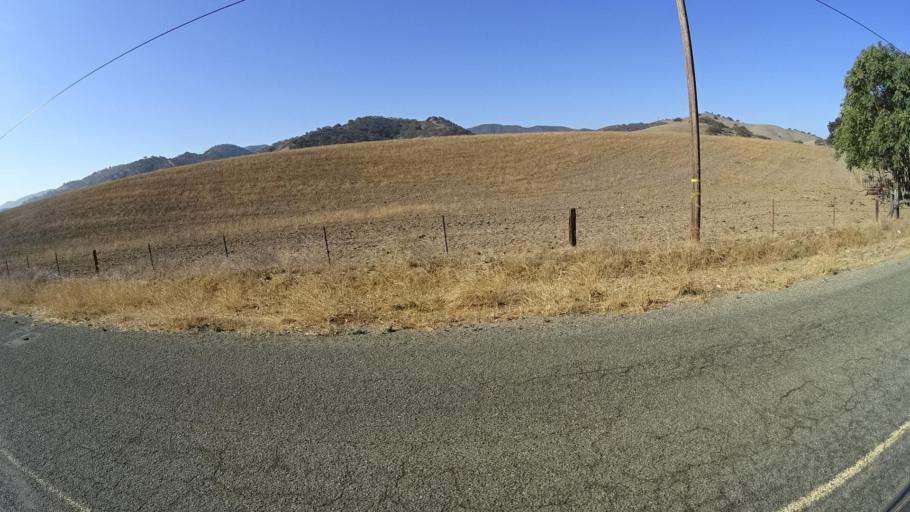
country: US
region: California
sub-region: Monterey County
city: King City
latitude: 36.0378
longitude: -120.9675
